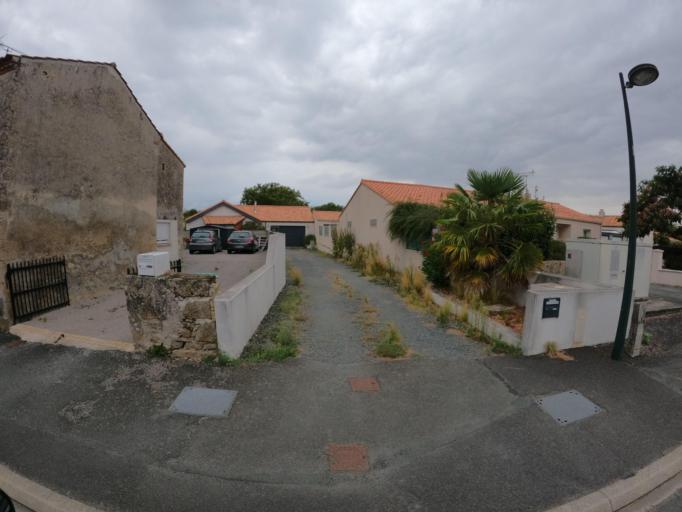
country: FR
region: Pays de la Loire
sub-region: Departement de la Vendee
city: La Boissiere-de-Montaigu
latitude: 46.9814
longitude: -1.1717
